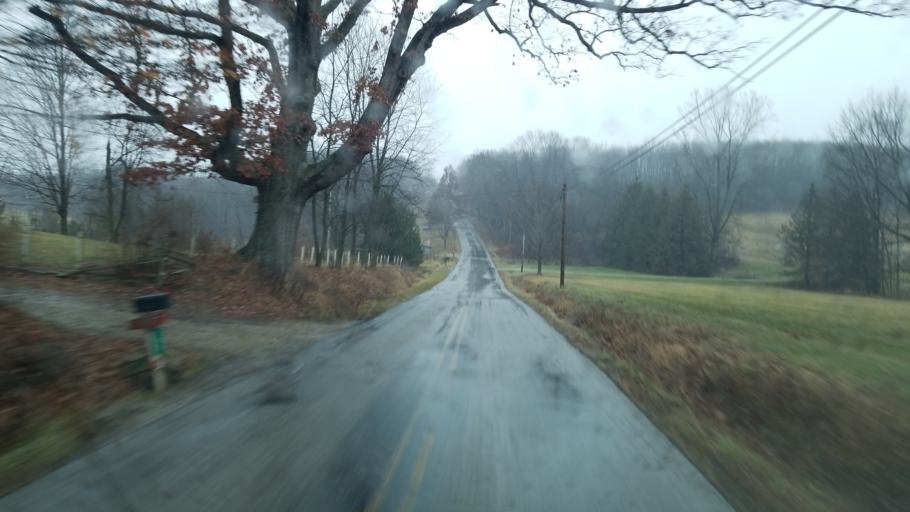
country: US
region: Ohio
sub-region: Licking County
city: Utica
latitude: 40.2173
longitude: -82.3369
